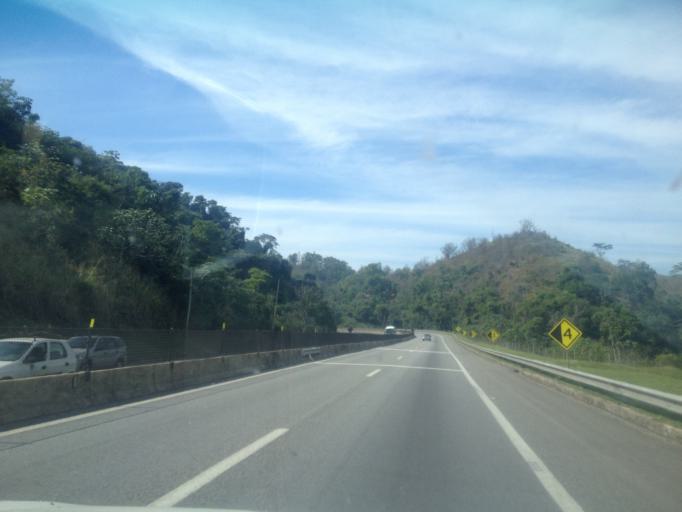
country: BR
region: Rio de Janeiro
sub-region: Pirai
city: Pirai
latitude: -22.6656
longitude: -43.8698
